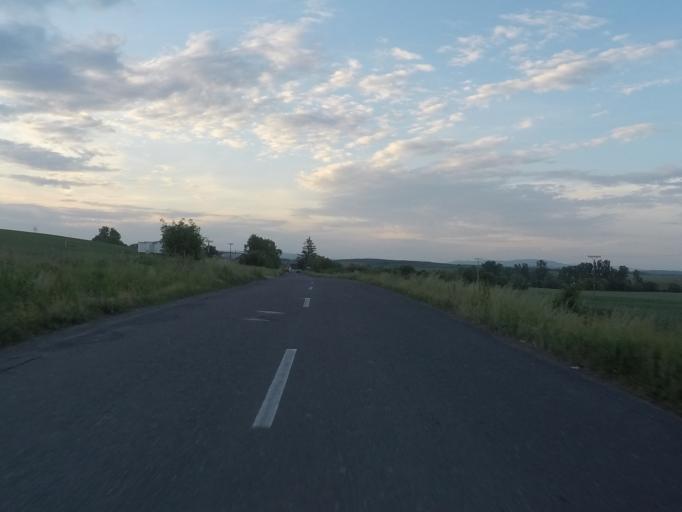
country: SK
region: Banskobystricky
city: Poltar
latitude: 48.3582
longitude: 19.8317
